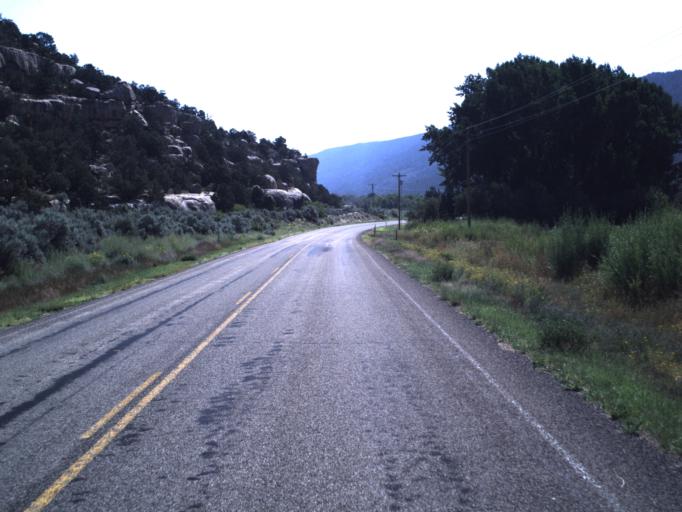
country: US
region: Utah
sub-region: Duchesne County
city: Duchesne
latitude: 40.3022
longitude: -110.6098
